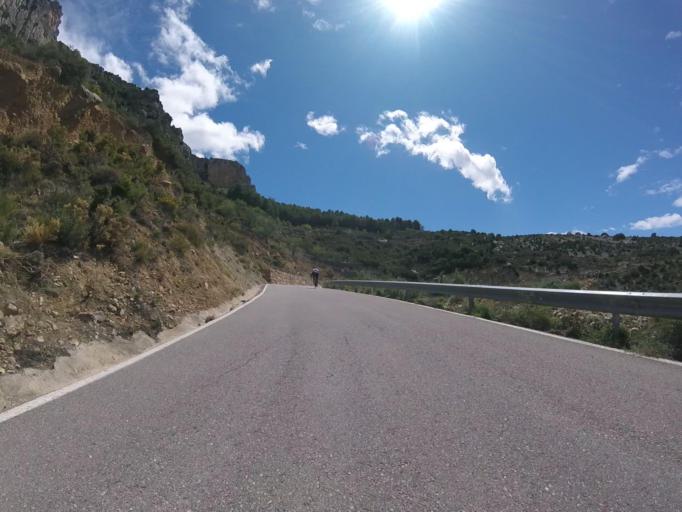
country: ES
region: Valencia
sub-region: Provincia de Castello
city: Sierra-Engarceran
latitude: 40.2829
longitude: -0.0323
